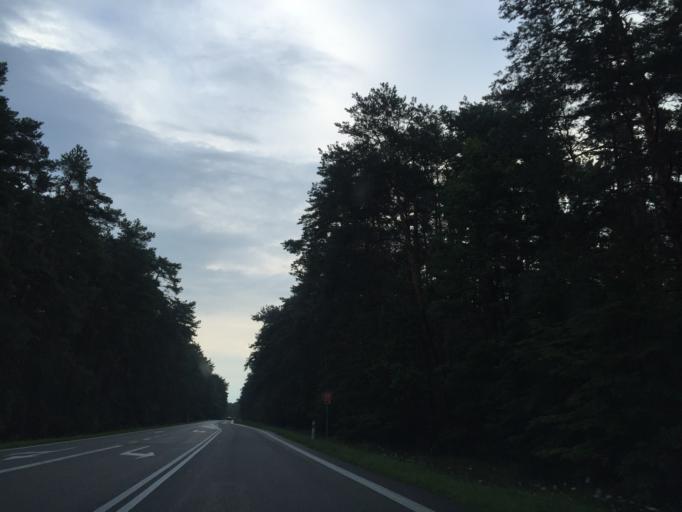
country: PL
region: Masovian Voivodeship
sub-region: Powiat ostrowski
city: Ostrow Mazowiecka
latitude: 52.7657
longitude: 21.8613
